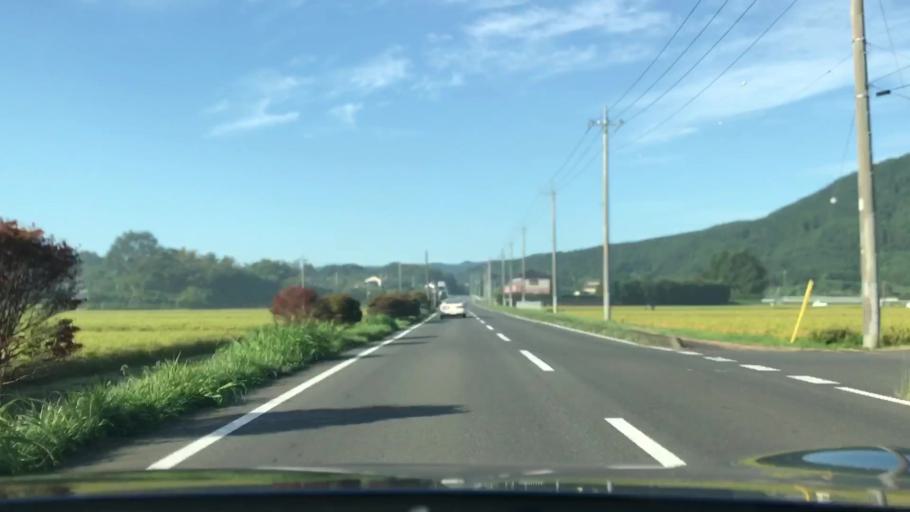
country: JP
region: Ibaraki
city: Makabe
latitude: 36.2568
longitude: 140.1710
